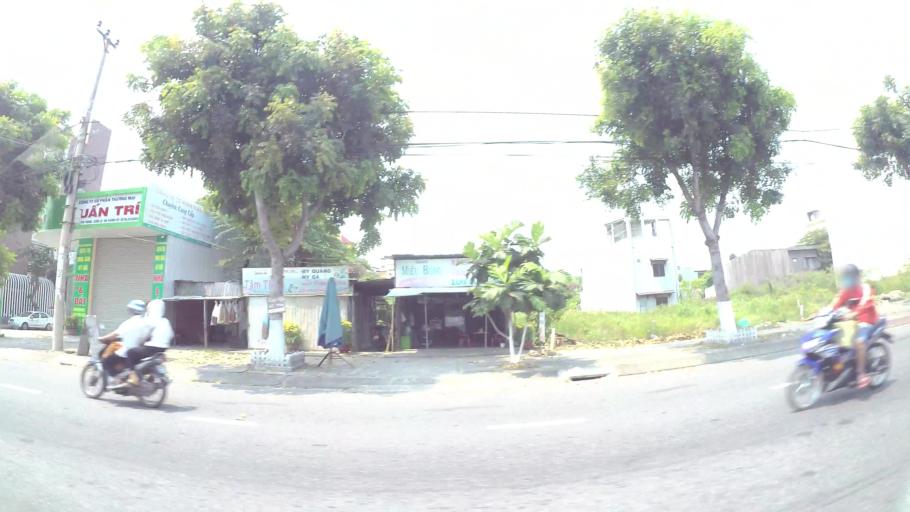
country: VN
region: Da Nang
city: Cam Le
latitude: 15.9868
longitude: 108.2078
